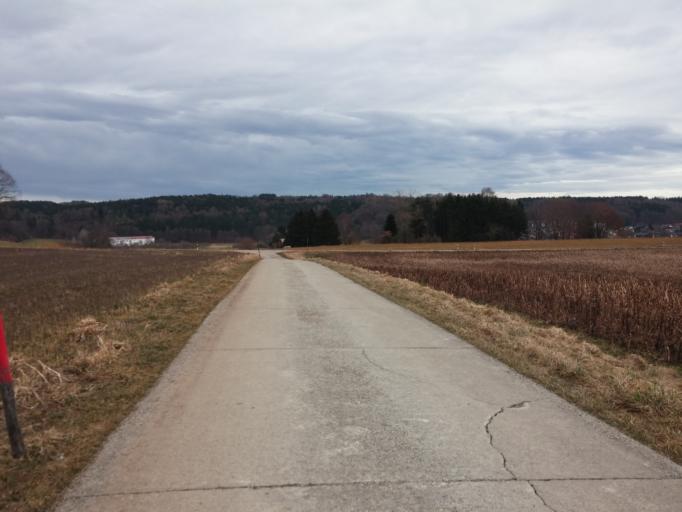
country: DE
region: Bavaria
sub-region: Upper Bavaria
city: Glonn
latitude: 47.9975
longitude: 11.8643
